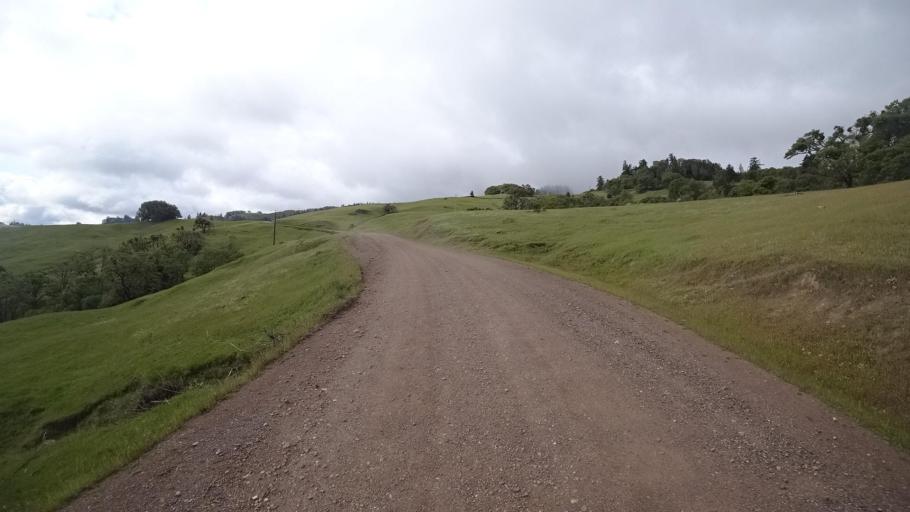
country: US
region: California
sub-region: Humboldt County
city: Redway
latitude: 40.2045
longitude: -123.6939
